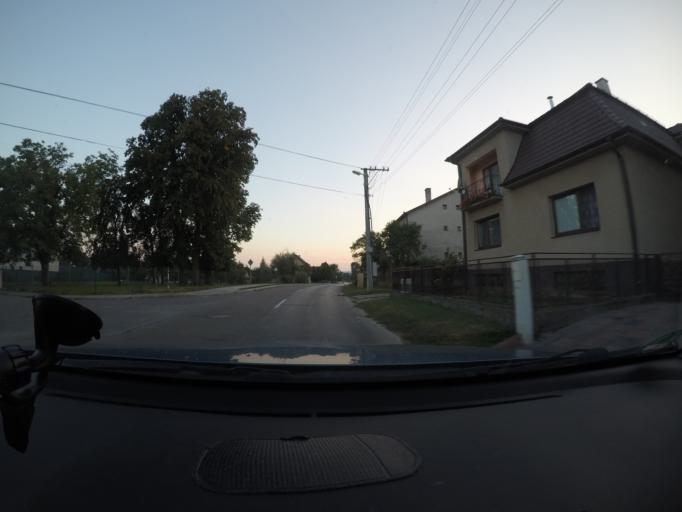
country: SK
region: Trenciansky
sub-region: Okres Trencin
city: Trencin
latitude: 48.8546
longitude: 17.9317
